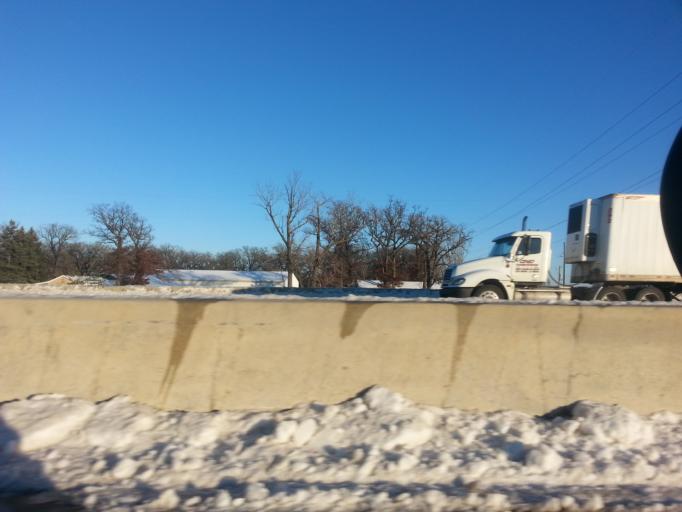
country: US
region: Wisconsin
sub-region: Kenosha County
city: Pleasant Prairie
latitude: 42.5062
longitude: -87.9516
